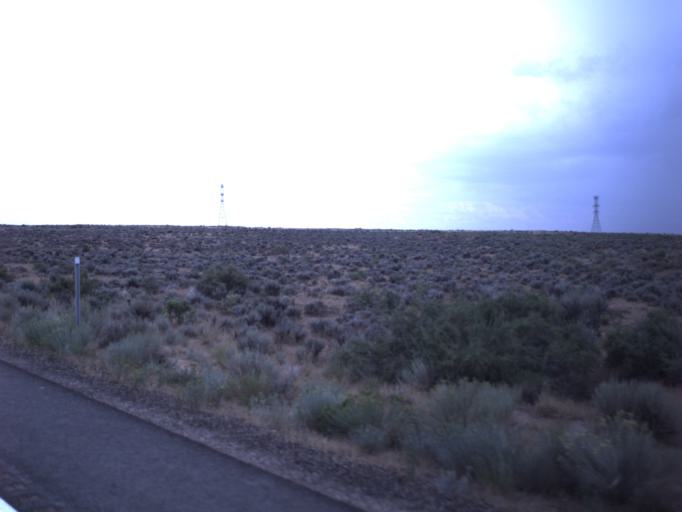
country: US
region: Utah
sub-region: Uintah County
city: Naples
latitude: 40.2364
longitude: -109.4132
